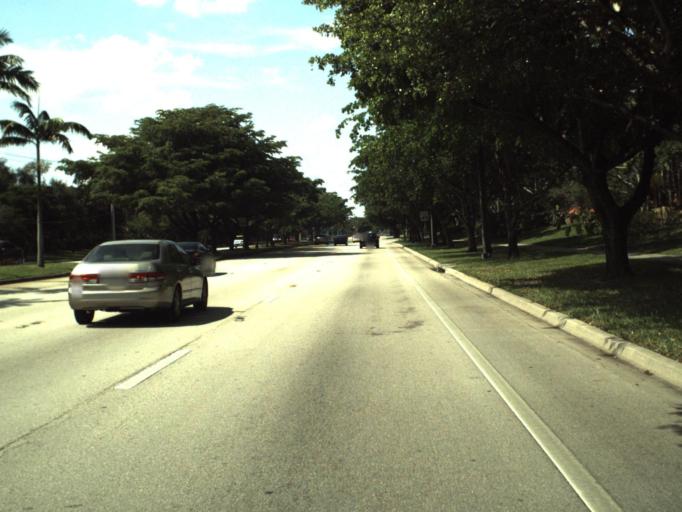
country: US
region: Florida
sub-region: Broward County
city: Plantation
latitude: 26.1300
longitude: -80.2565
